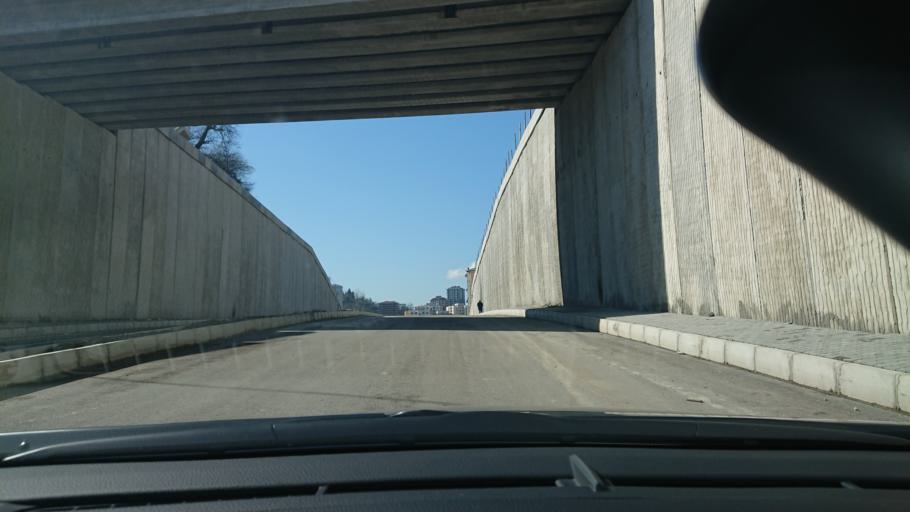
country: TR
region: Rize
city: Rize
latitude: 41.0186
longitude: 40.5211
